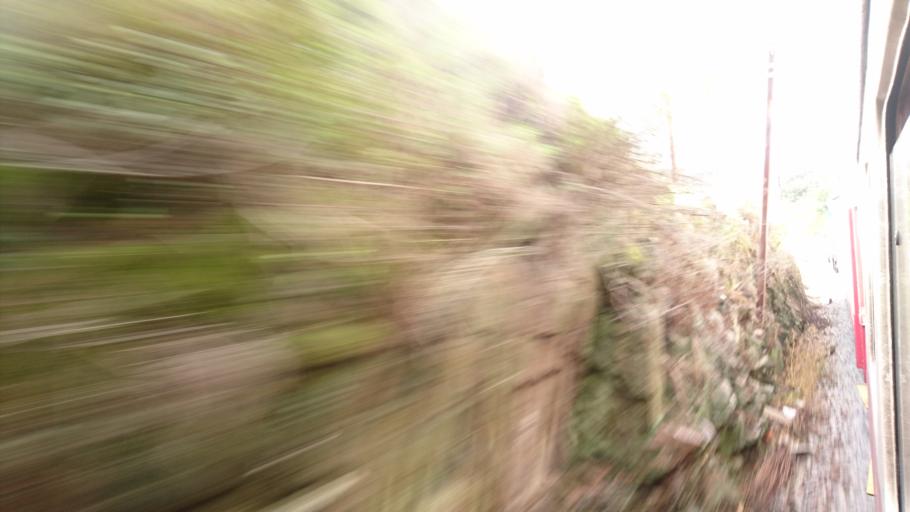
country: PT
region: Viseu
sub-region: Cinfaes
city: Cinfaes
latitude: 41.0940
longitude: -8.0744
